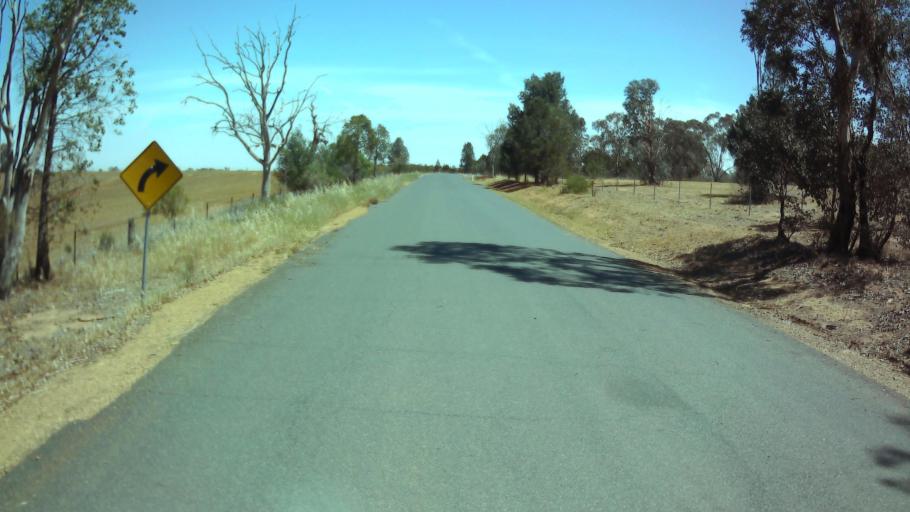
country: AU
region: New South Wales
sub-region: Weddin
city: Grenfell
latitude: -33.9046
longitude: 148.1827
